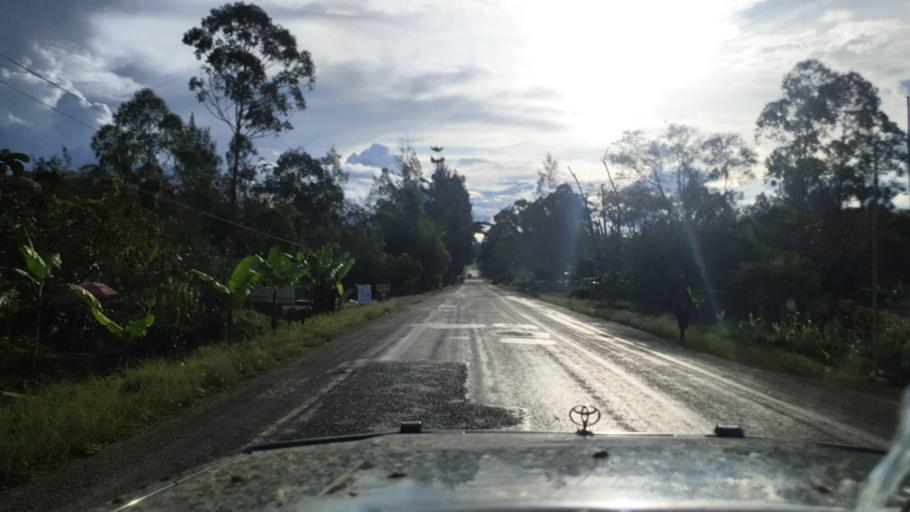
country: PG
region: Jiwaka
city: Minj
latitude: -5.8352
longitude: 144.5547
